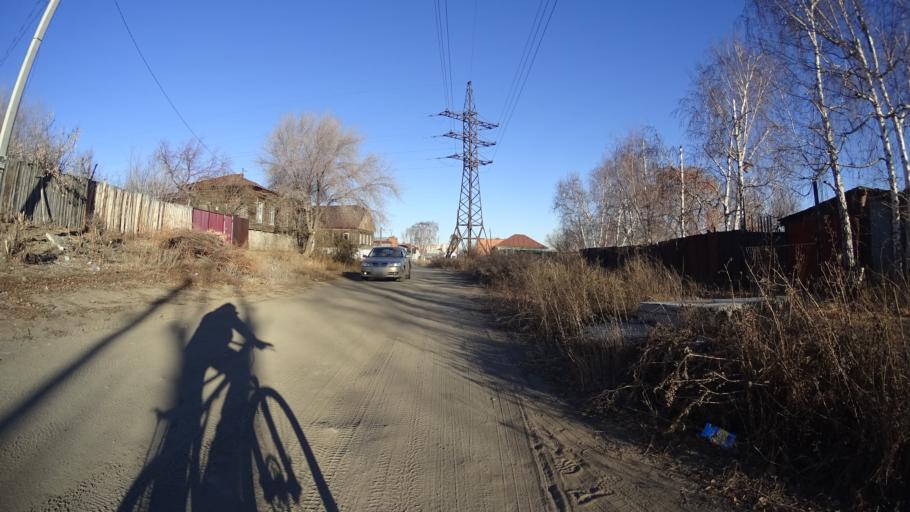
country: RU
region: Chelyabinsk
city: Troitsk
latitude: 54.0811
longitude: 61.5669
